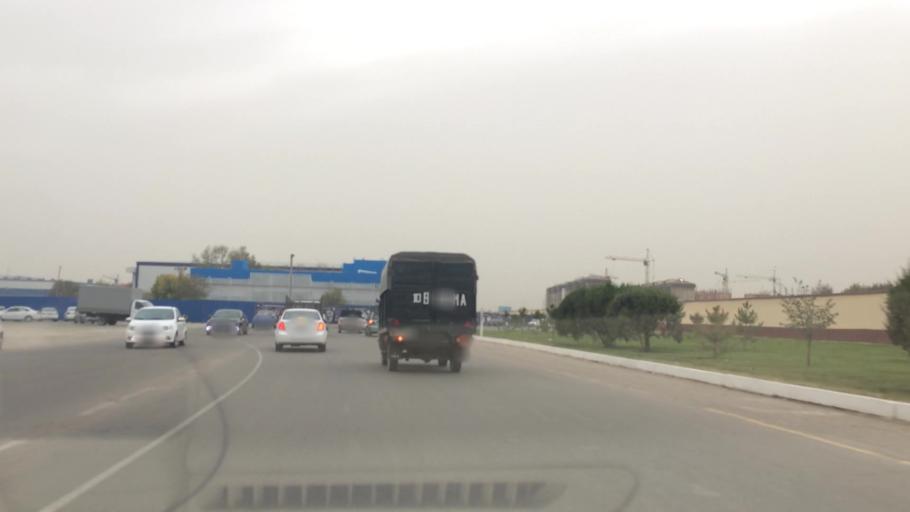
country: UZ
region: Toshkent
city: Salor
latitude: 41.3055
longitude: 69.3372
